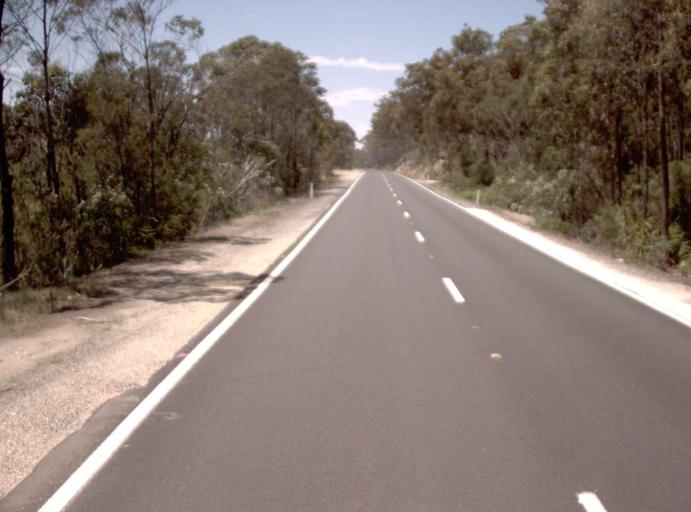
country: AU
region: Victoria
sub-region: East Gippsland
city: Lakes Entrance
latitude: -37.7118
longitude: 148.6702
